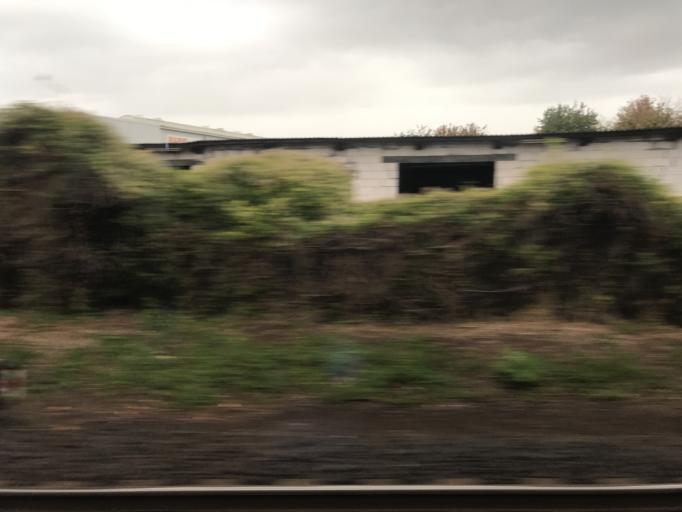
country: DE
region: Hesse
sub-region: Regierungsbezirk Darmstadt
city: Riedstadt
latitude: 49.8359
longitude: 8.4912
